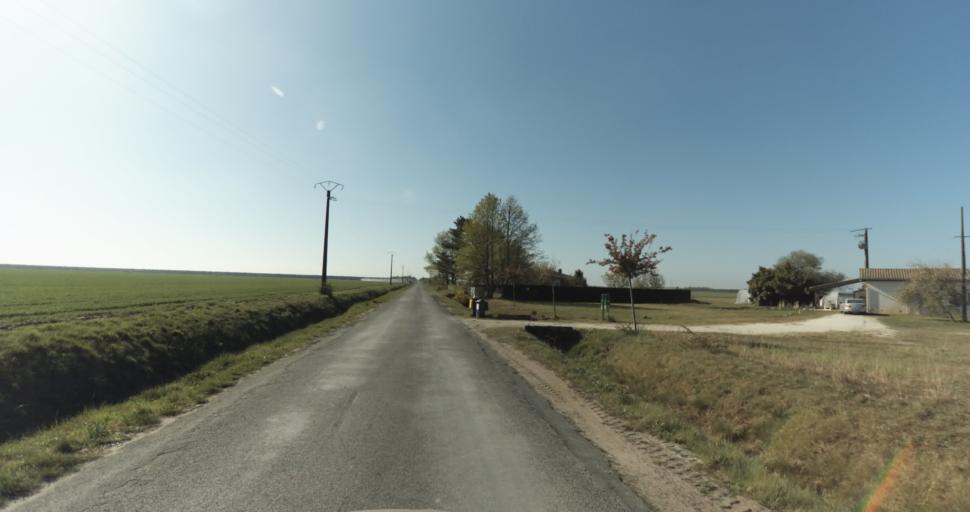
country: FR
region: Aquitaine
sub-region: Departement de la Gironde
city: Marcheprime
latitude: 44.7749
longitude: -0.8585
